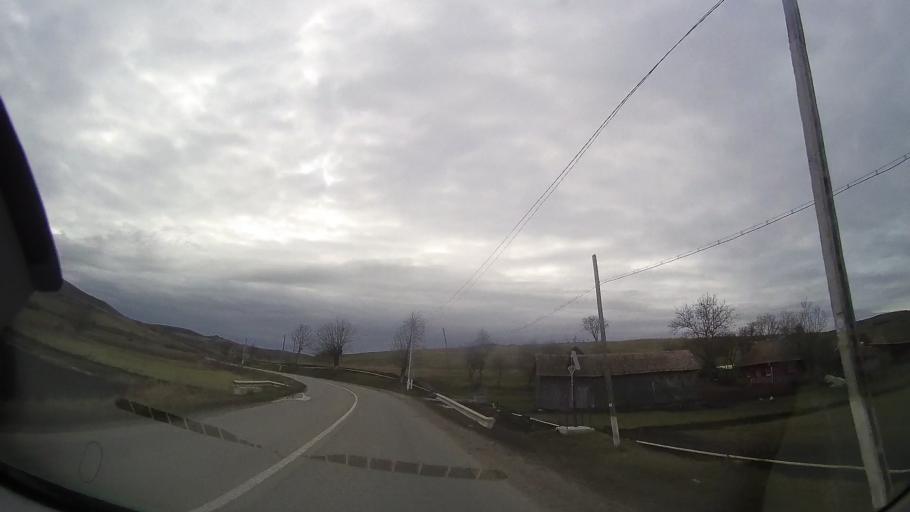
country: RO
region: Bistrita-Nasaud
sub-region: Comuna Budesti
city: Budesti
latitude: 46.8602
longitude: 24.2429
